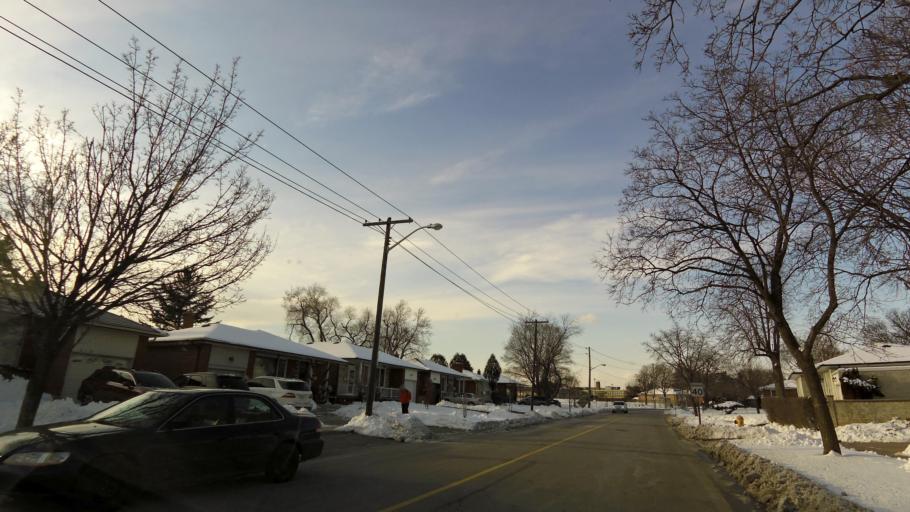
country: CA
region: Ontario
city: Etobicoke
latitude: 43.6582
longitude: -79.5784
